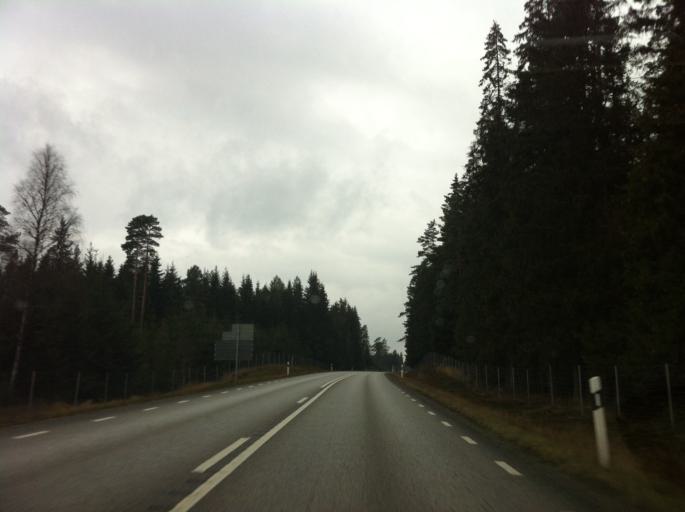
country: SE
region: Joenkoeping
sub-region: Savsjo Kommun
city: Saevsjoe
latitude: 57.3880
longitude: 14.6115
